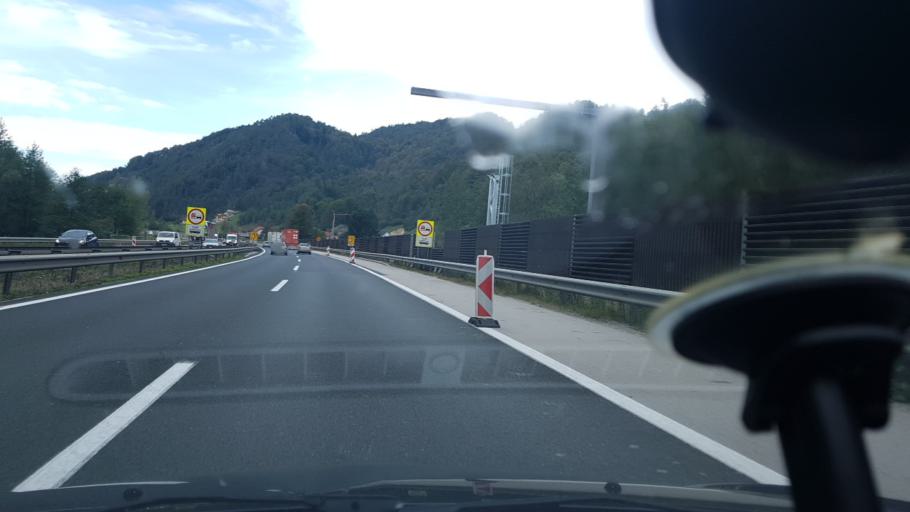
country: SI
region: Moravce
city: Moravce
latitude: 46.1691
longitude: 14.7368
